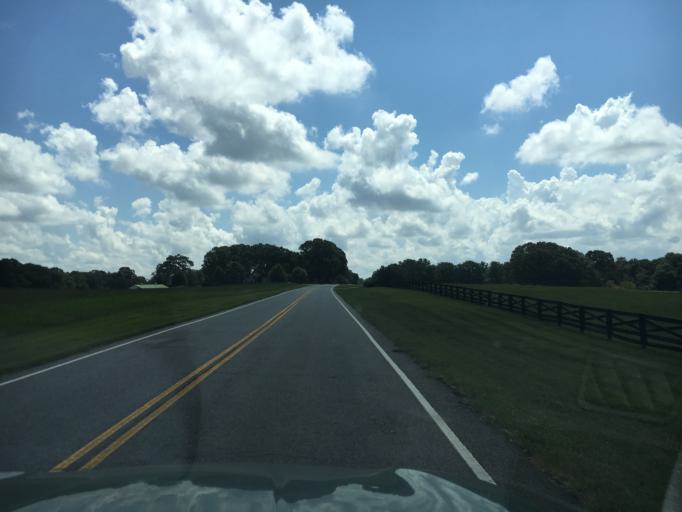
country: US
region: South Carolina
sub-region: Spartanburg County
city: Fairforest
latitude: 34.9046
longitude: -82.0419
